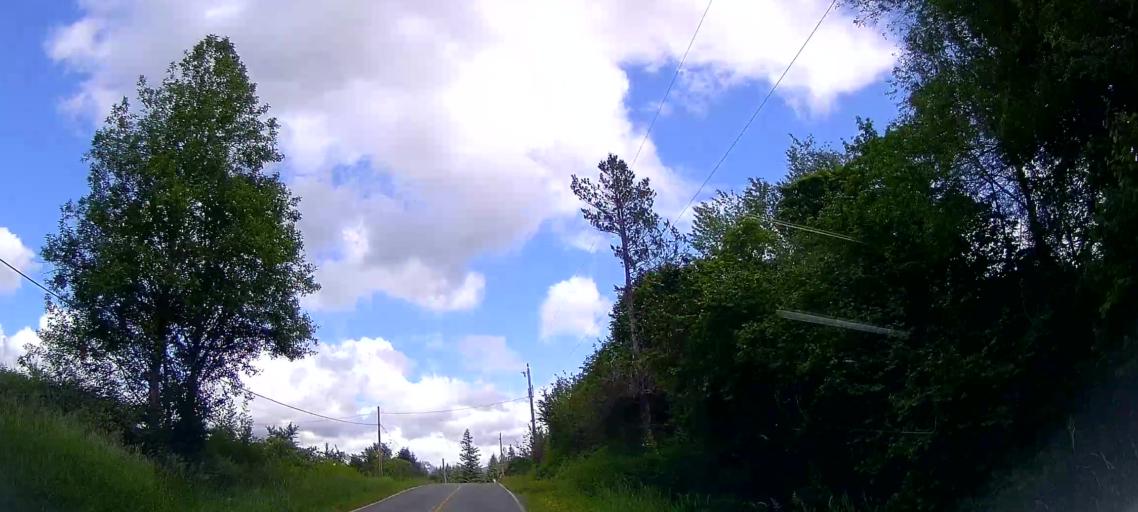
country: US
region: Washington
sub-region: Whatcom County
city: Sudden Valley
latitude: 48.6785
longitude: -122.1931
